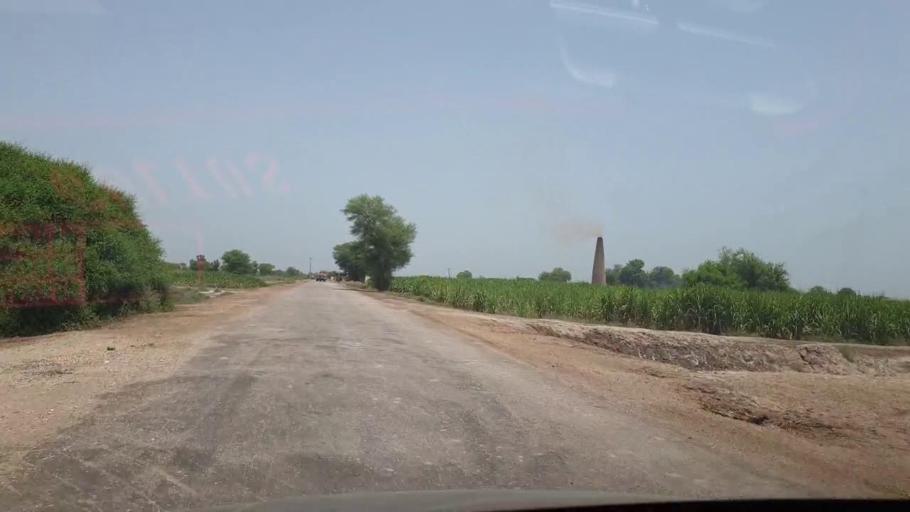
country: PK
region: Sindh
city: Daulatpur
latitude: 26.3894
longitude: 68.0874
